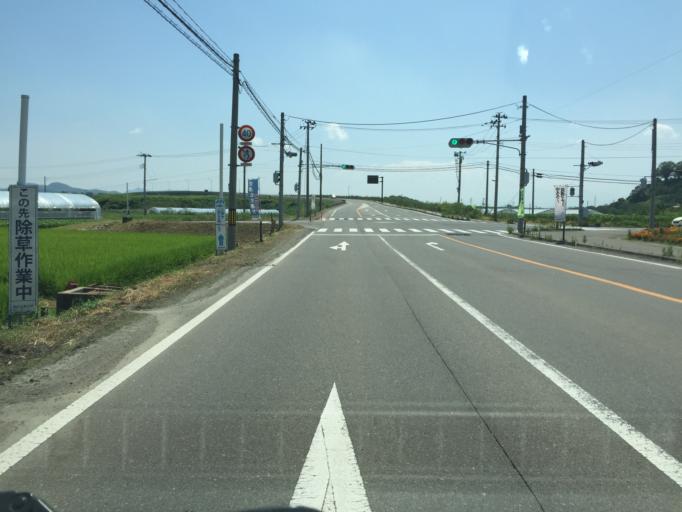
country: JP
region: Fukushima
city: Yanagawamachi-saiwaicho
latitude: 37.8741
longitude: 140.6097
